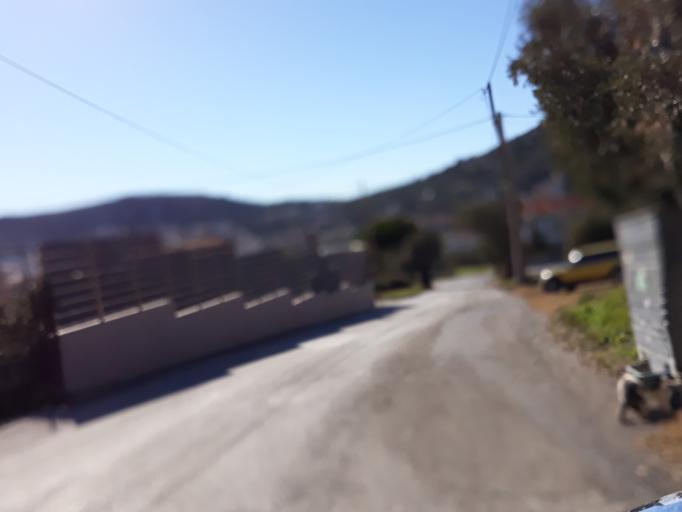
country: GR
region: Attica
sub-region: Nomarchia Dytikis Attikis
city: Fyli
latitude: 38.1099
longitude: 23.6719
